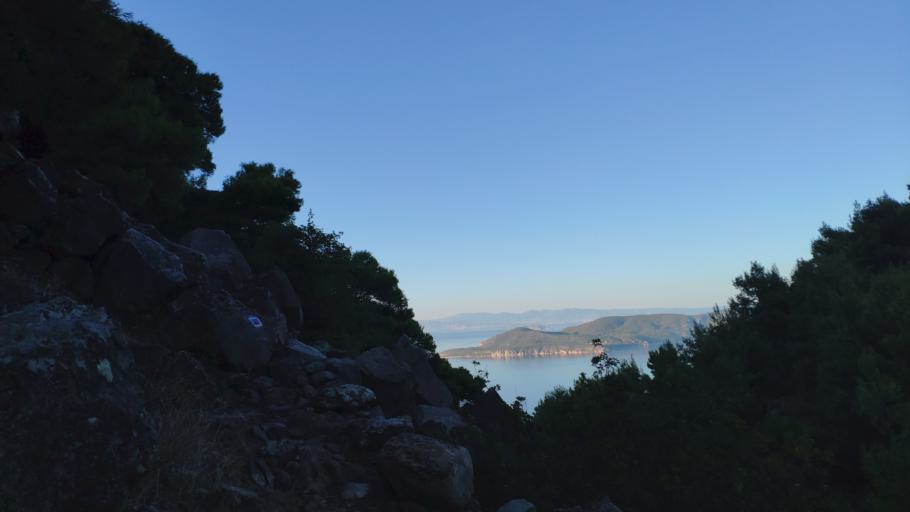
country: GR
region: Attica
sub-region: Nomos Piraios
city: Megalochori
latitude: 37.6190
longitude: 23.3355
